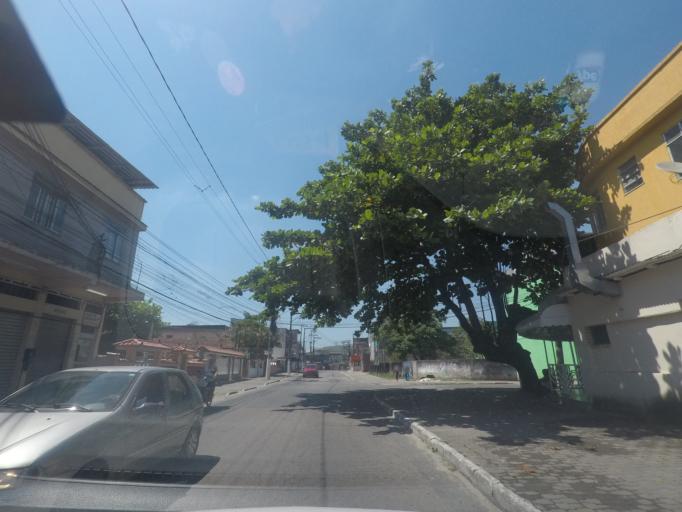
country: BR
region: Rio de Janeiro
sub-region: Petropolis
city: Petropolis
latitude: -22.5854
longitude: -43.1862
